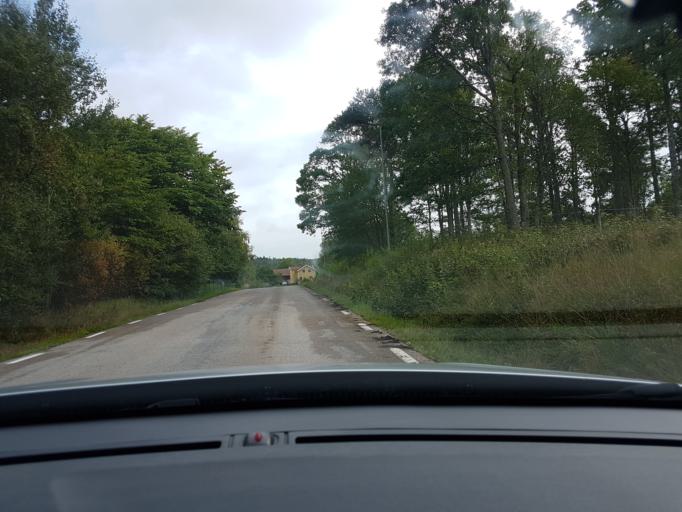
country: SE
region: Vaestra Goetaland
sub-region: Ale Kommun
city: Alvangen
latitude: 57.9162
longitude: 12.1429
